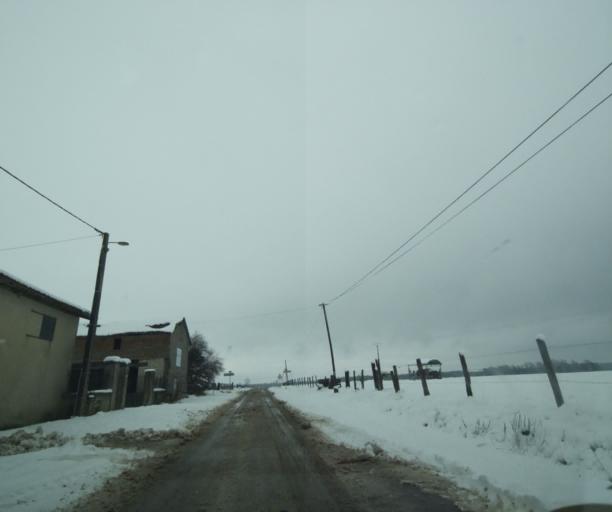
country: FR
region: Champagne-Ardenne
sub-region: Departement de la Haute-Marne
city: Montier-en-Der
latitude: 48.5112
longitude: 4.7787
